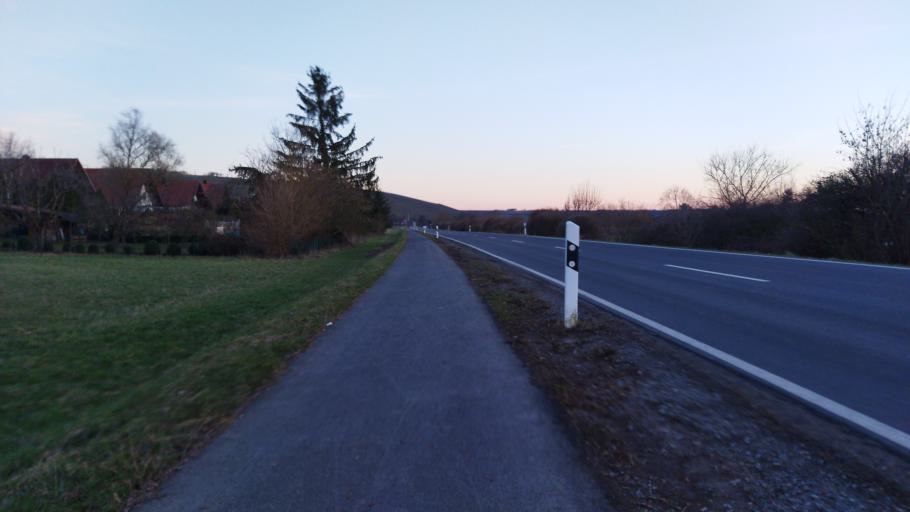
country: DE
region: Bavaria
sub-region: Regierungsbezirk Unterfranken
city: Wipfeld
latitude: 49.9093
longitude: 10.1892
